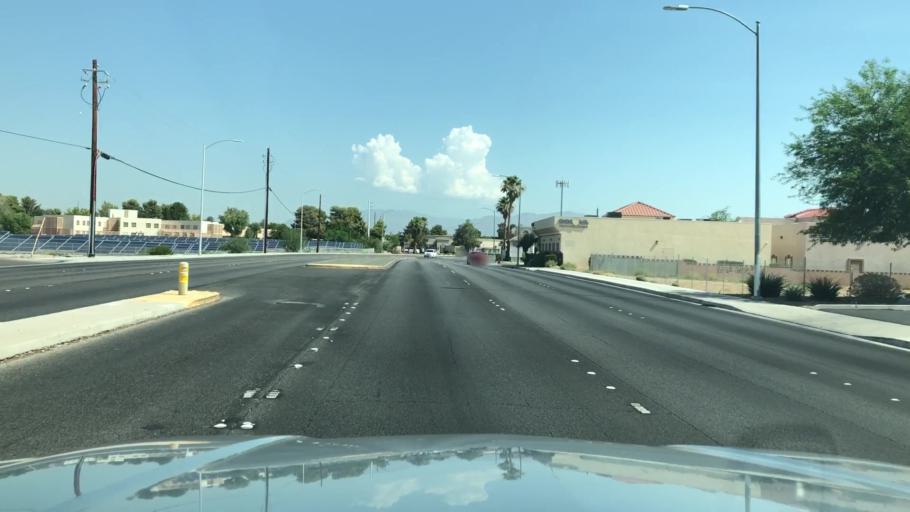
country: US
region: Nevada
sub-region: Clark County
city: Spring Valley
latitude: 36.1543
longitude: -115.2257
